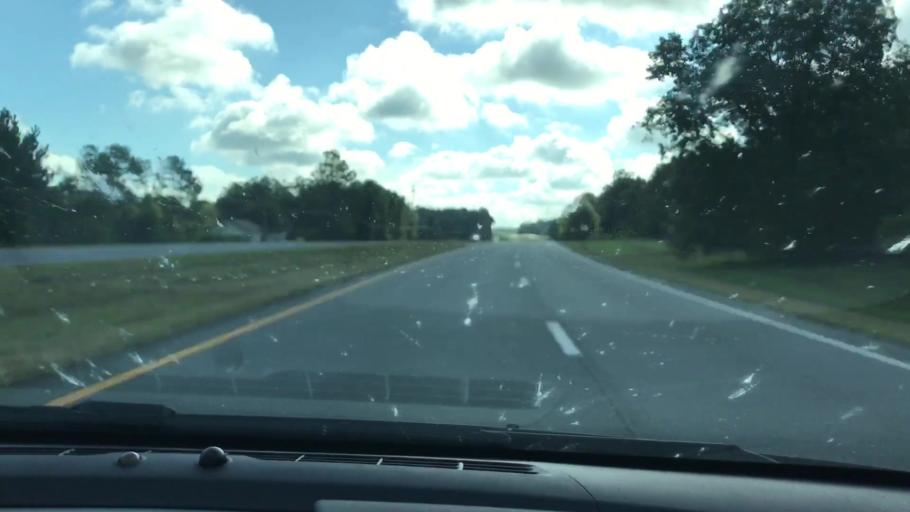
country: US
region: Georgia
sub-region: Worth County
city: Sylvester
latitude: 31.5524
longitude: -83.9495
